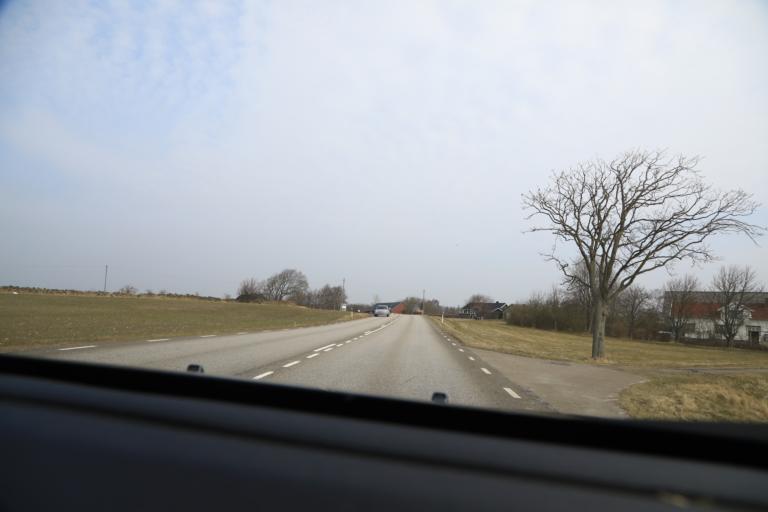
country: SE
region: Halland
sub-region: Kungsbacka Kommun
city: Frillesas
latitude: 57.2657
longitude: 12.1791
